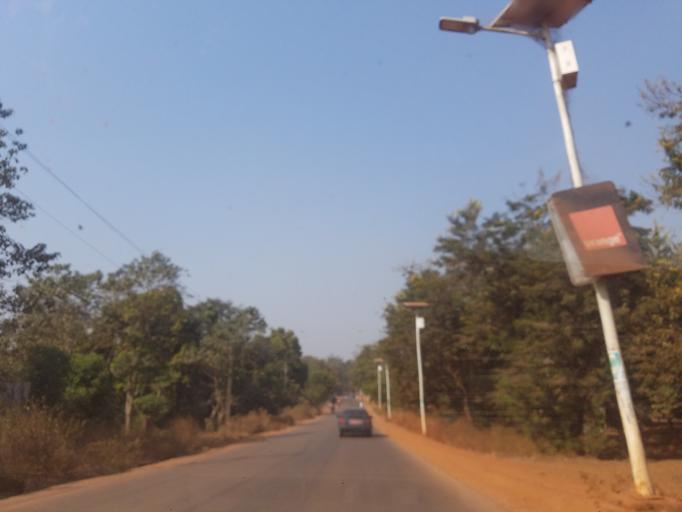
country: GN
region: Boke
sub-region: Boke Prefecture
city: Boke
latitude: 10.9206
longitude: -14.2954
